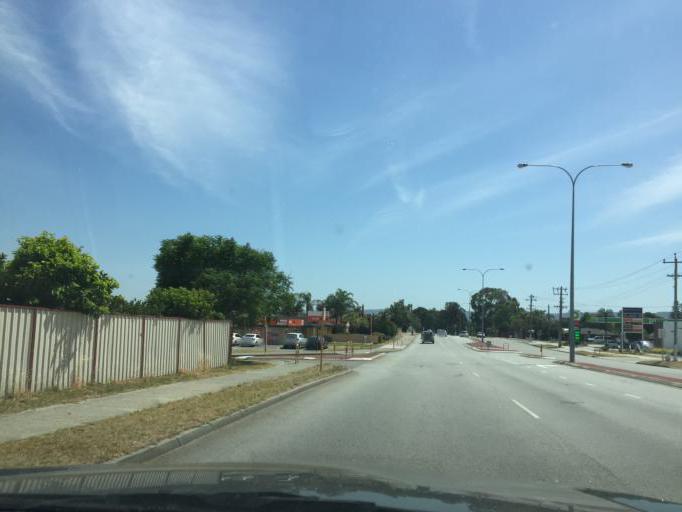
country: AU
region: Western Australia
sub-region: Gosnells
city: Thornlie
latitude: -32.0719
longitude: 115.9653
